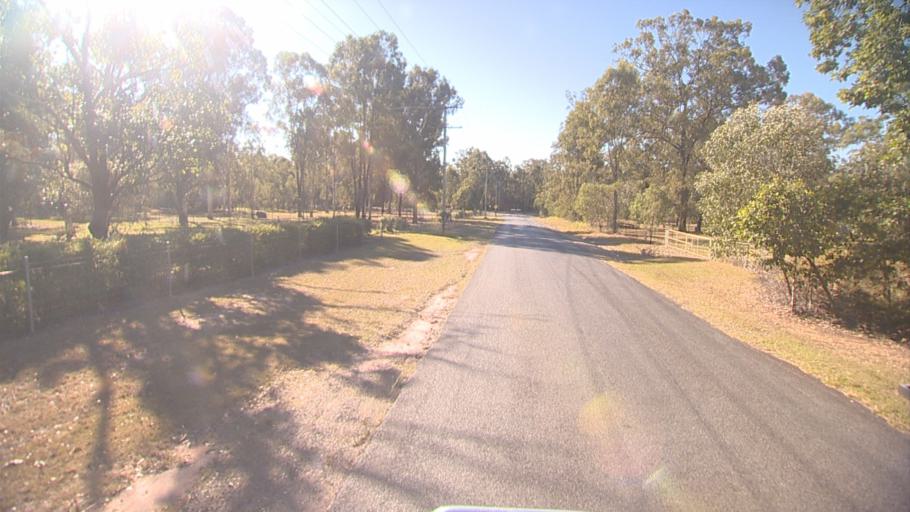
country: AU
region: Queensland
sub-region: Logan
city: Park Ridge South
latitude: -27.7251
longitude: 153.0204
